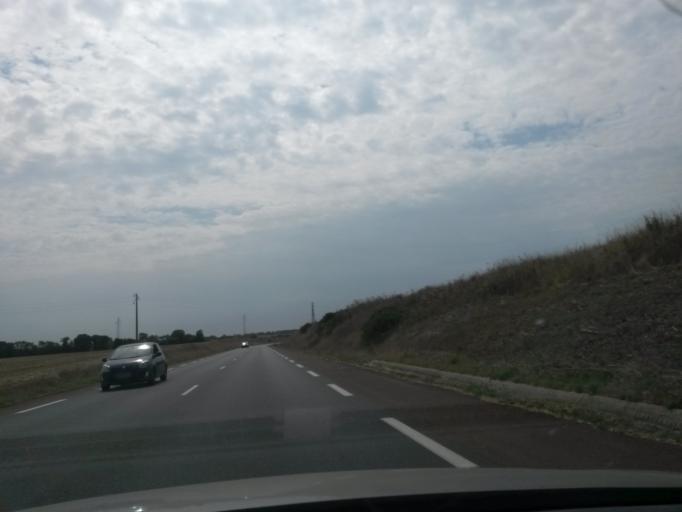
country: FR
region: Poitou-Charentes
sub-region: Departement de la Charente-Maritime
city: Saint-Xandre
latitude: 46.2109
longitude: -1.0904
